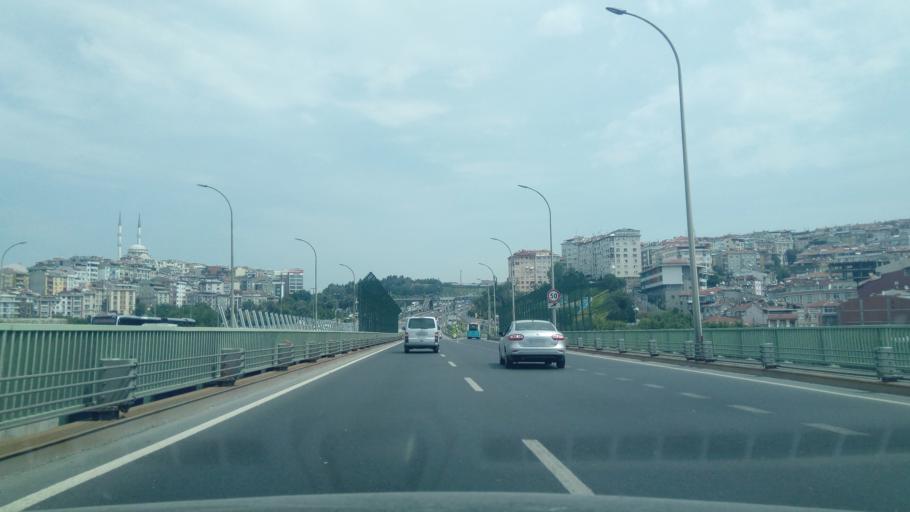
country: TR
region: Istanbul
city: Istanbul
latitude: 41.0432
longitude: 28.9420
